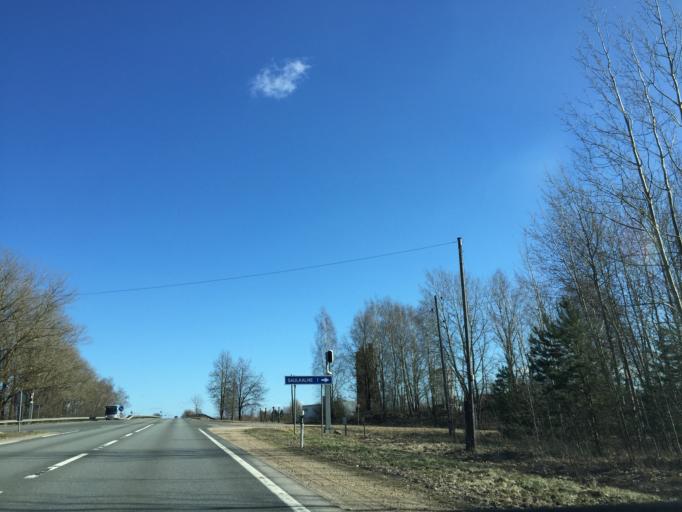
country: LV
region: Salaspils
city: Salaspils
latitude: 56.8466
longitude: 24.4210
